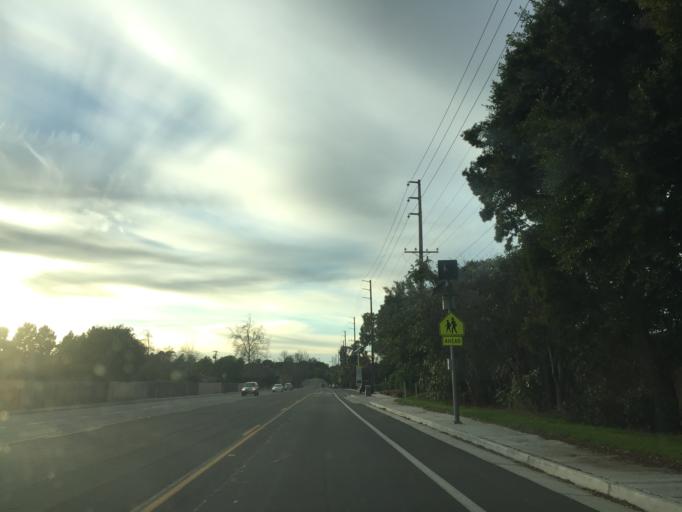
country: US
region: California
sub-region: Santa Barbara County
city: Goleta
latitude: 34.4515
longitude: -119.7977
